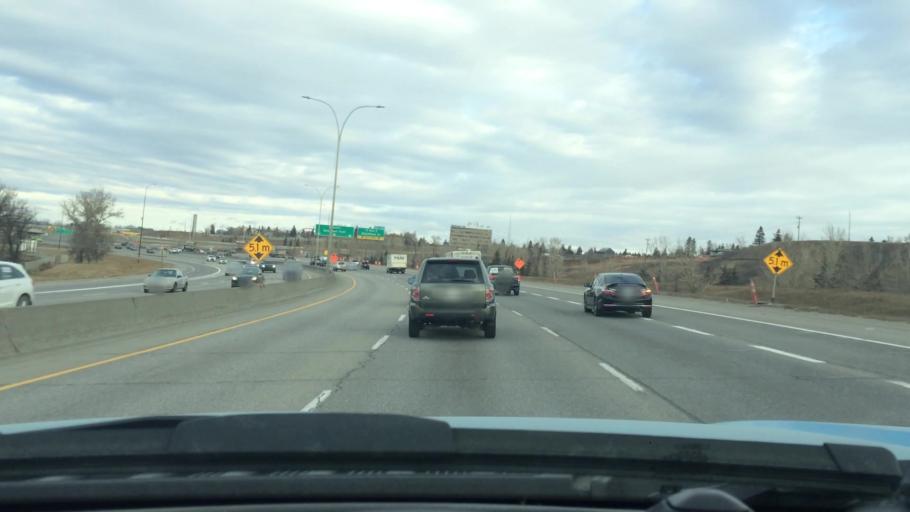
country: CA
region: Alberta
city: Calgary
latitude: 51.0311
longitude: -113.9974
